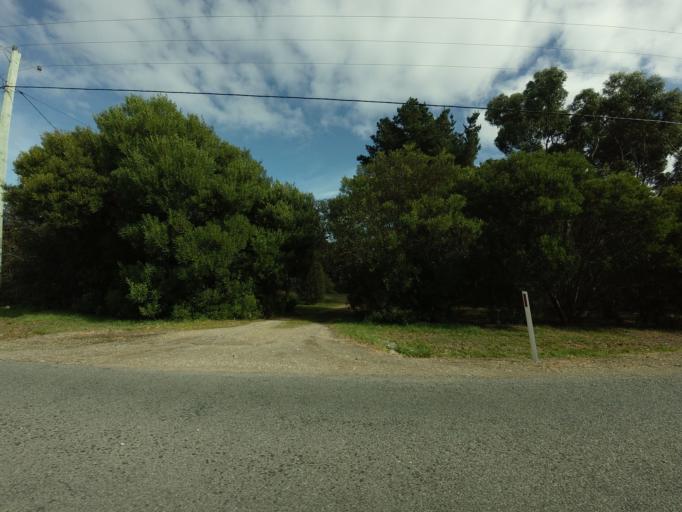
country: AU
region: Tasmania
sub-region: Clarence
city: Sandford
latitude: -43.0884
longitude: 147.7380
